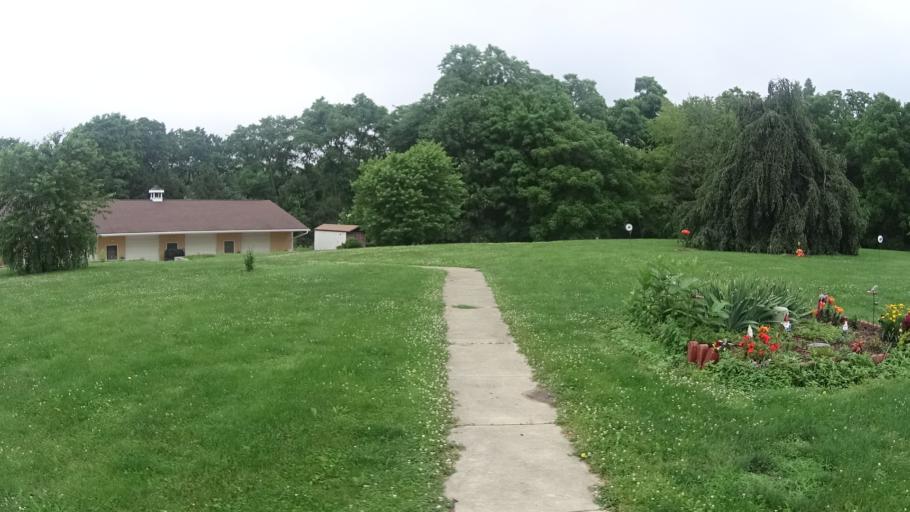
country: US
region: Ohio
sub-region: Erie County
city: Huron
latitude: 41.3277
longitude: -82.4875
